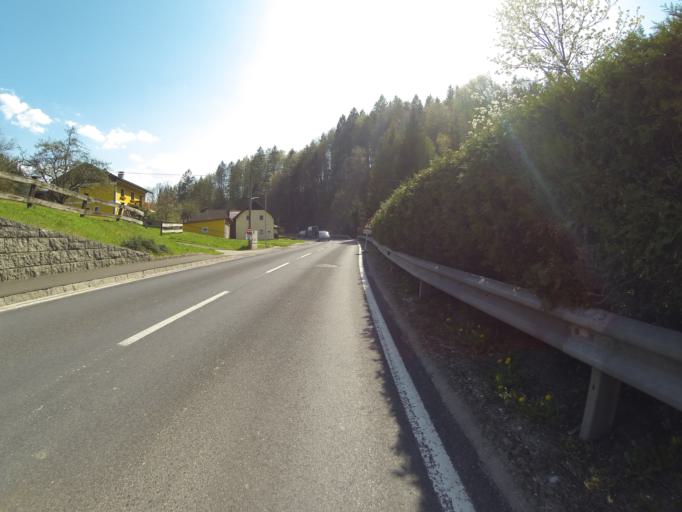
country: AT
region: Upper Austria
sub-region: Politischer Bezirk Gmunden
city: Altmunster
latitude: 47.9060
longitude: 13.7094
